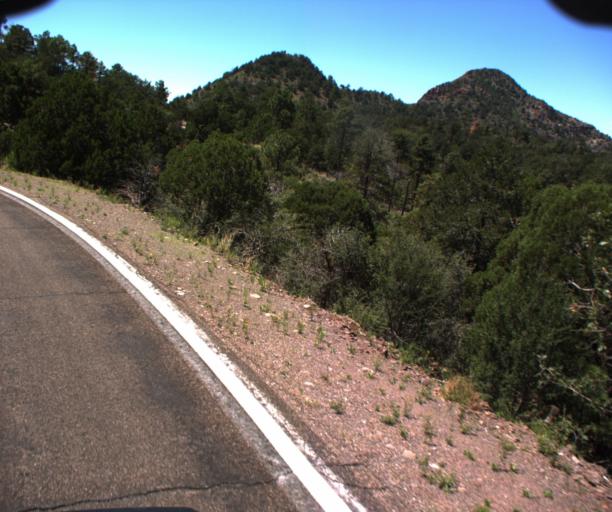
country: US
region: Arizona
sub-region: Greenlee County
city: Morenci
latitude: 33.2299
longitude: -109.3915
